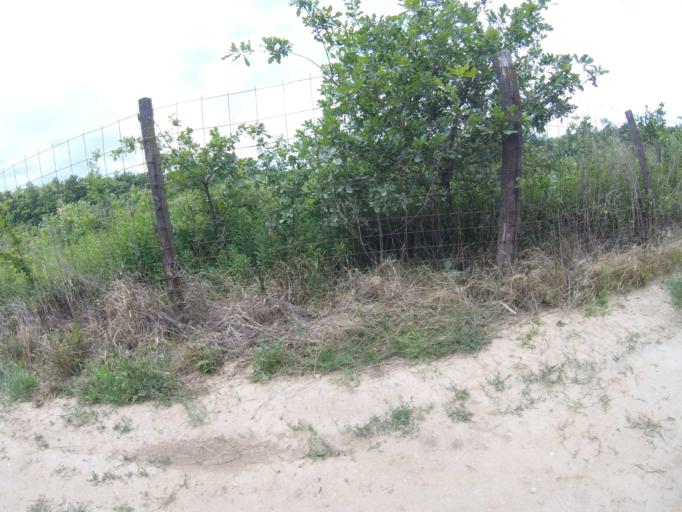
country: HU
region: Zala
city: Turje
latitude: 47.0399
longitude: 17.0785
